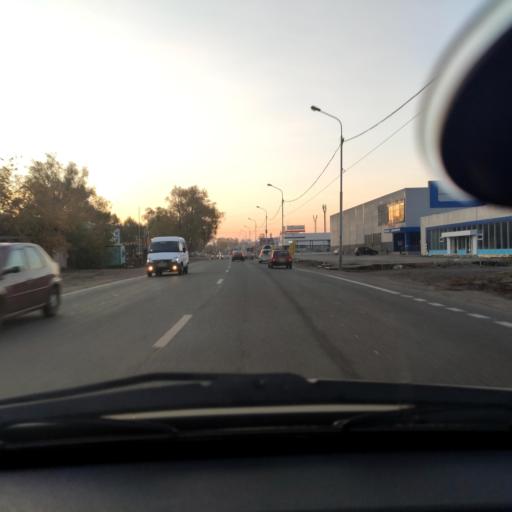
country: RU
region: Bashkortostan
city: Ufa
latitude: 54.6915
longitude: 55.9816
